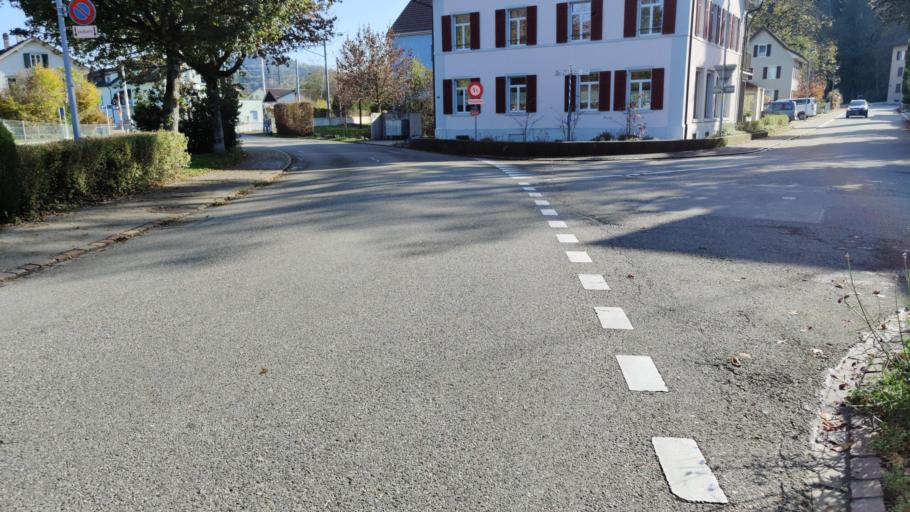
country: CH
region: Zurich
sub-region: Bezirk Pfaeffikon
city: Wila
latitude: 47.4175
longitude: 8.8486
